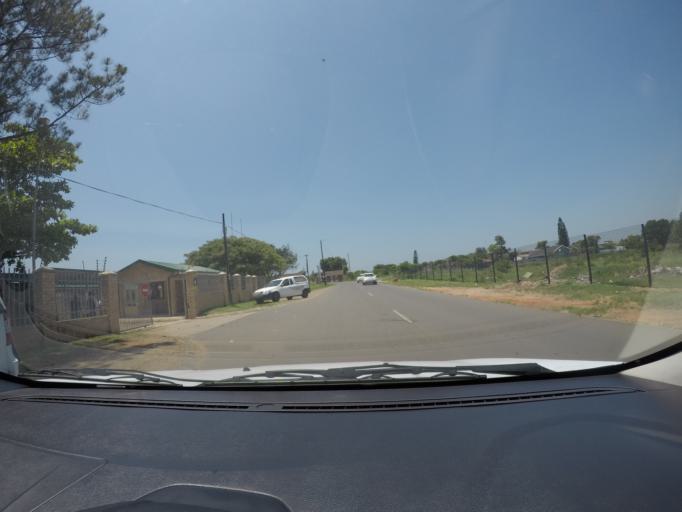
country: ZA
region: KwaZulu-Natal
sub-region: uThungulu District Municipality
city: eSikhawini
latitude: -28.8690
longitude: 31.9094
